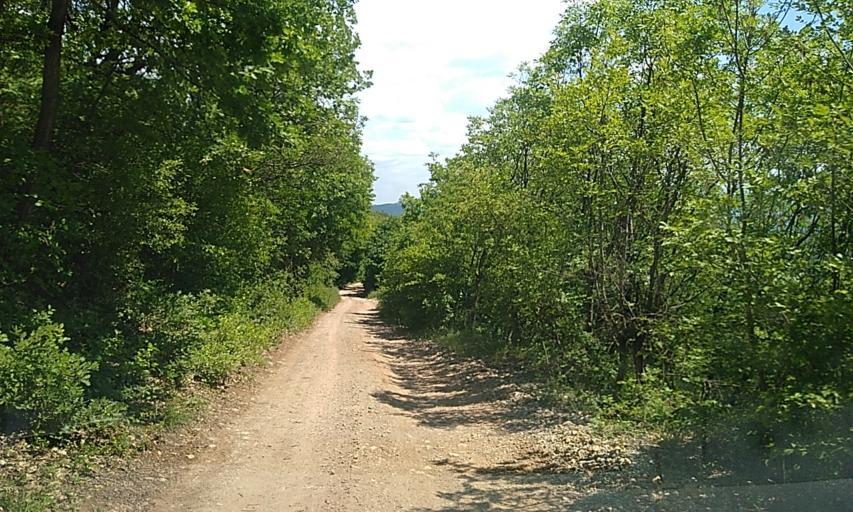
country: RS
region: Central Serbia
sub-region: Nisavski Okrug
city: Niska Banja
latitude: 43.3706
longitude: 21.9929
